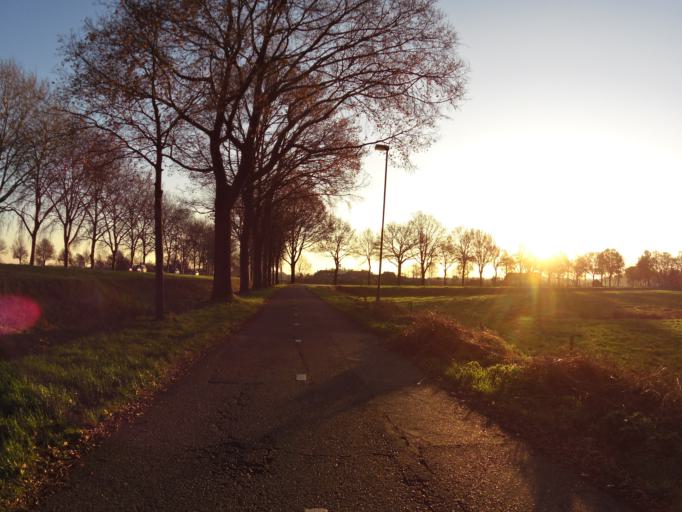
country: NL
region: North Brabant
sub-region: Gemeente Sint-Michielsgestel
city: Sint-Michielsgestel
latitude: 51.6478
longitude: 5.3245
